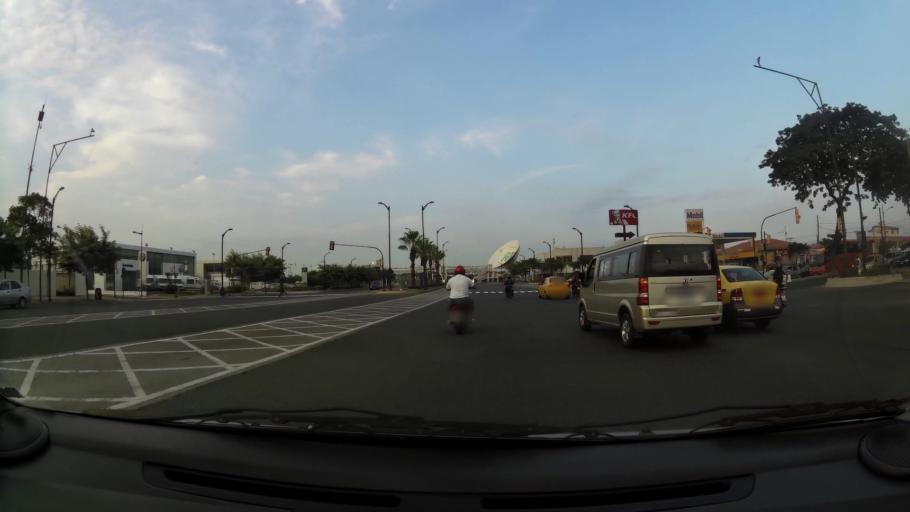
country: EC
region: Guayas
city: Eloy Alfaro
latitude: -2.1453
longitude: -79.8852
